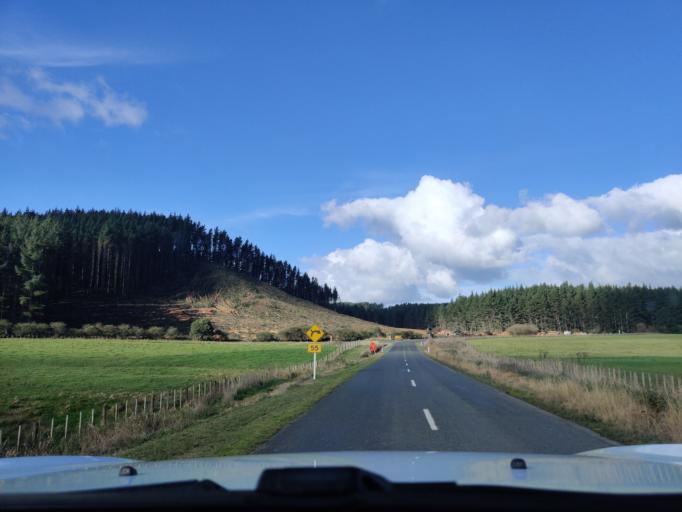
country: NZ
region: Waikato
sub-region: Waikato District
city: Te Kauwhata
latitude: -37.2922
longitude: 175.2255
